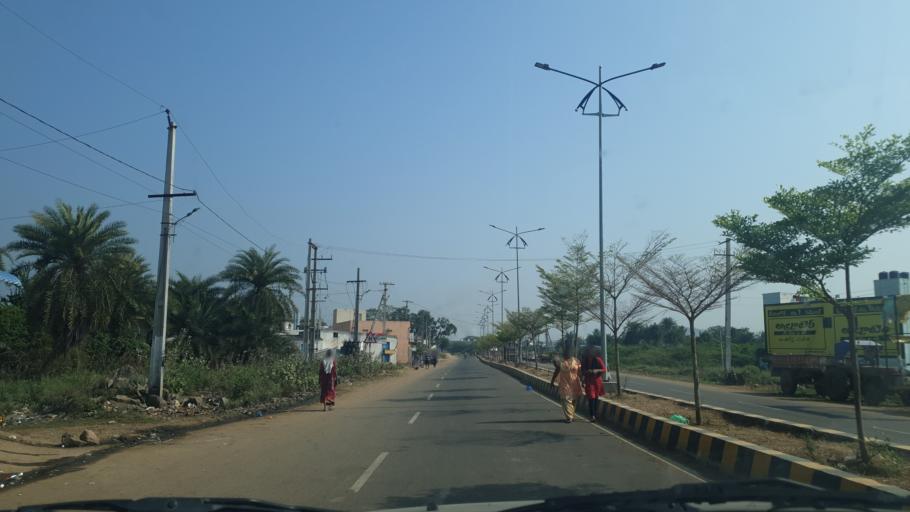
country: IN
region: Andhra Pradesh
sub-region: Srikakulam
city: Tekkali
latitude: 18.6120
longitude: 84.2344
